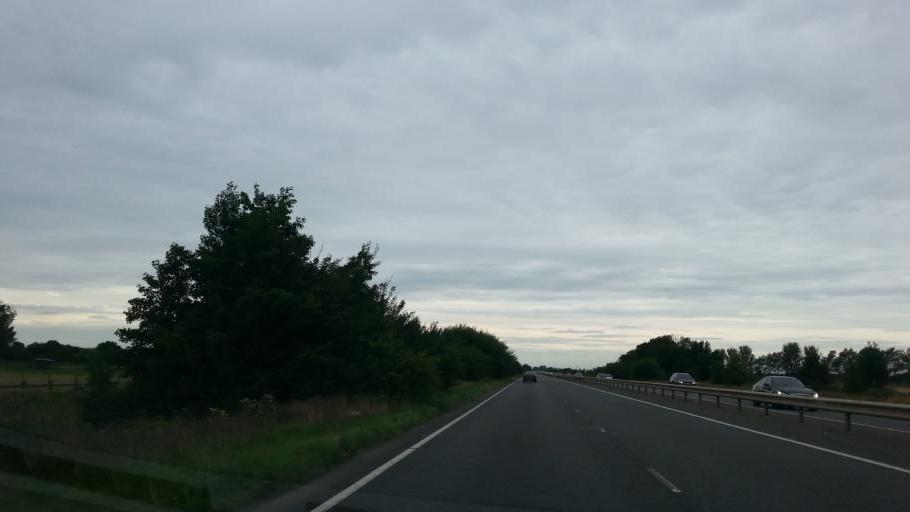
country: GB
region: England
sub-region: Peterborough
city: Thorney
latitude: 52.6222
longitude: -0.0701
